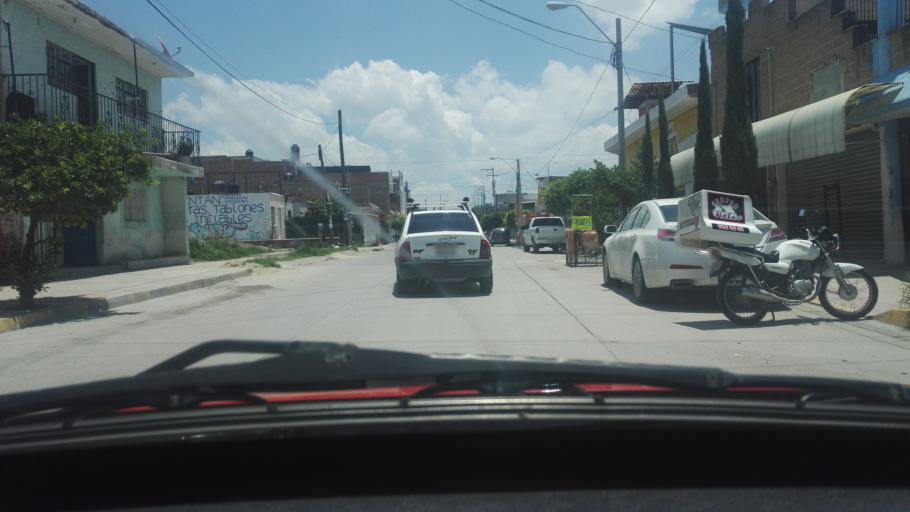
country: MX
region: Guanajuato
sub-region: Leon
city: San Jose de Duran (Los Troncoso)
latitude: 21.0813
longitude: -101.6345
